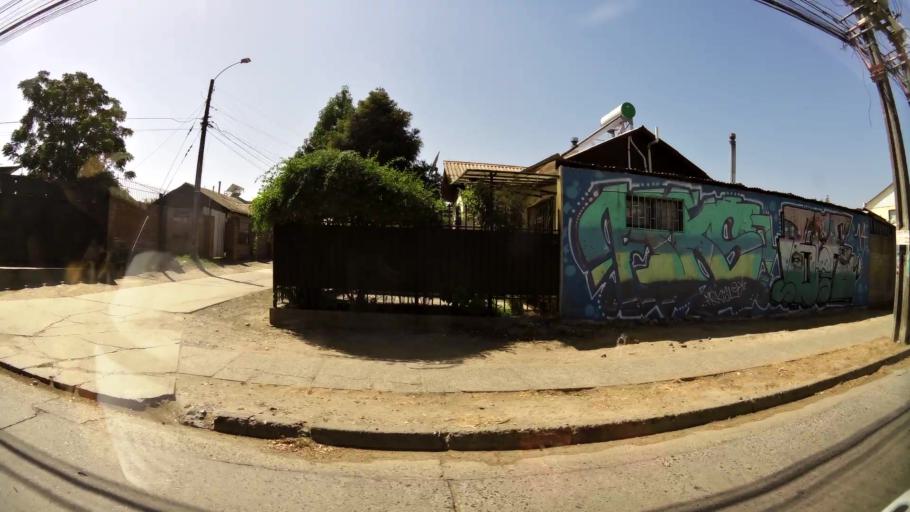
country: CL
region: Maule
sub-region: Provincia de Talca
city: Talca
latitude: -35.4207
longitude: -71.6446
